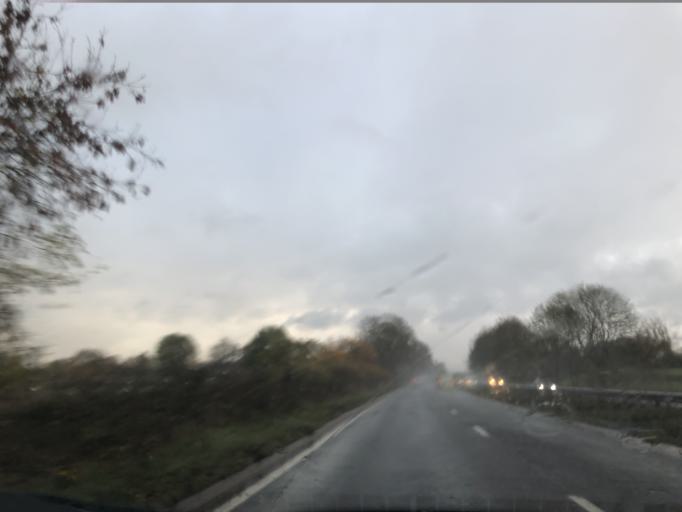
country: GB
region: England
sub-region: Solihull
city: Meriden
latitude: 52.4402
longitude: -1.6231
